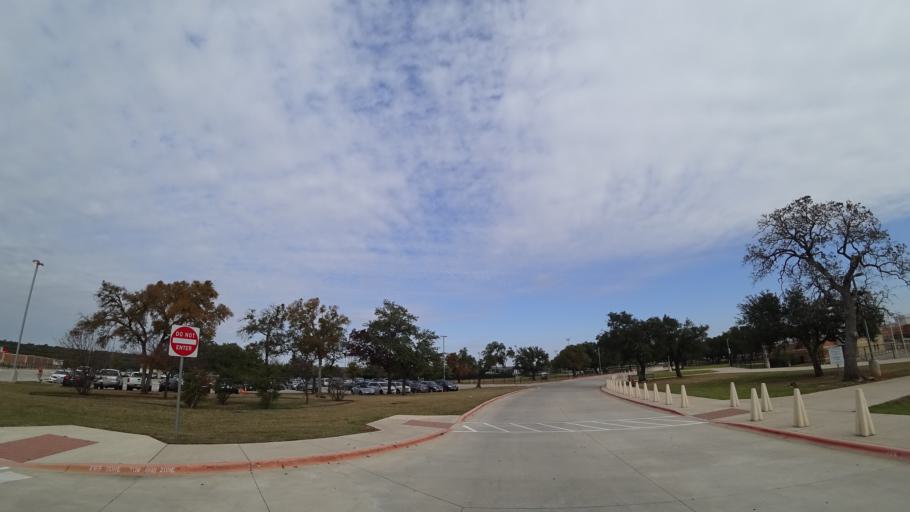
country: US
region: Texas
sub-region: Williamson County
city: Anderson Mill
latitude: 30.3970
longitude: -97.8287
